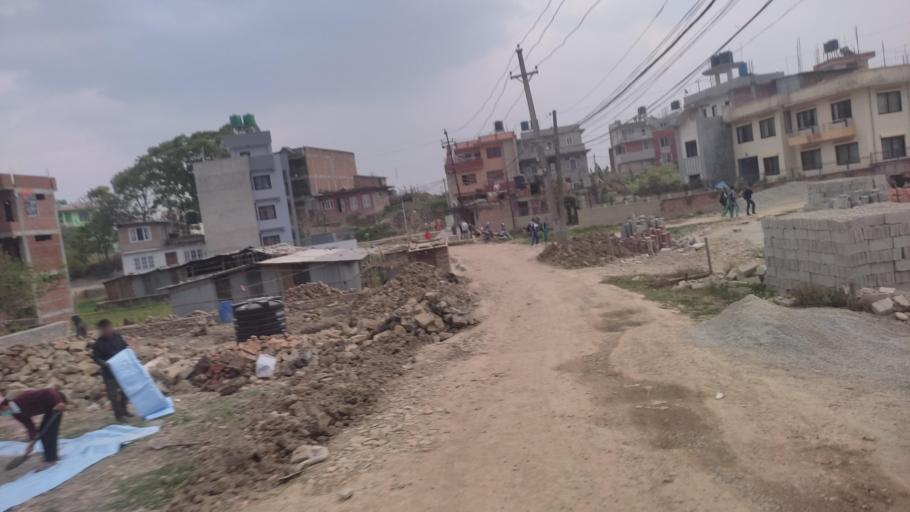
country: NP
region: Central Region
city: Kirtipur
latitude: 27.6659
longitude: 85.2700
